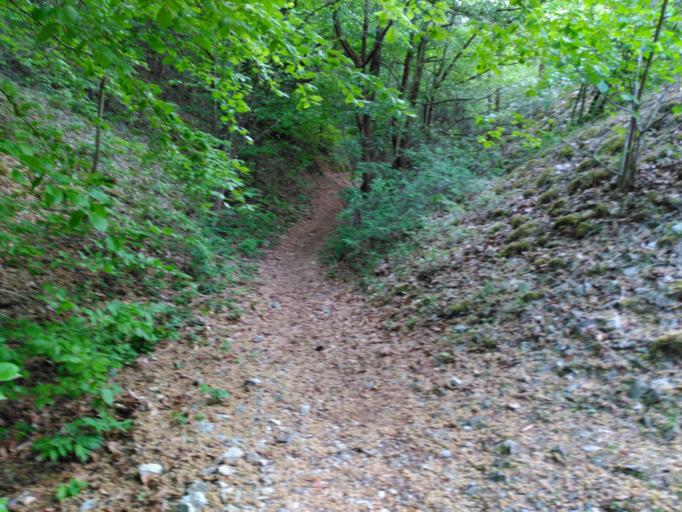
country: CZ
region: Central Bohemia
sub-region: Okres Beroun
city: Kraluv Dvur
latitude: 49.9187
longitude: 14.0590
